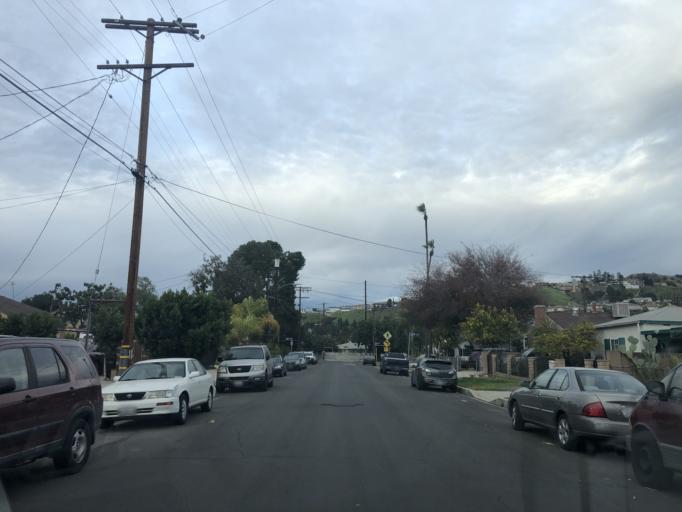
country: US
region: California
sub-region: Los Angeles County
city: North Hollywood
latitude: 34.2130
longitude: -118.3534
